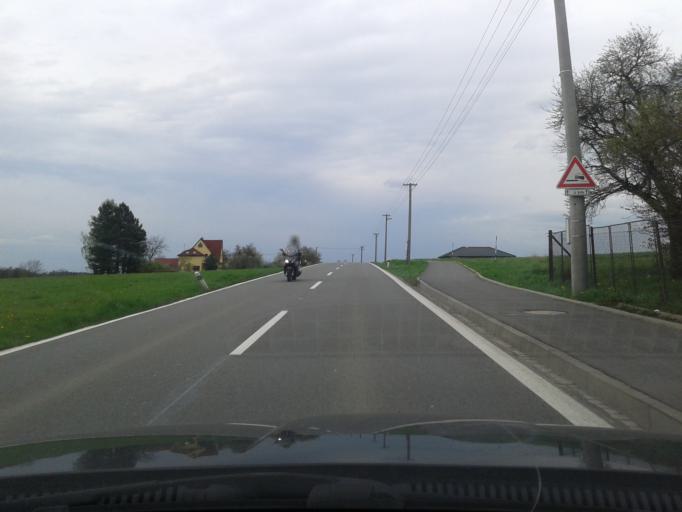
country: CZ
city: Sedliste
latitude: 49.7218
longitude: 18.3685
